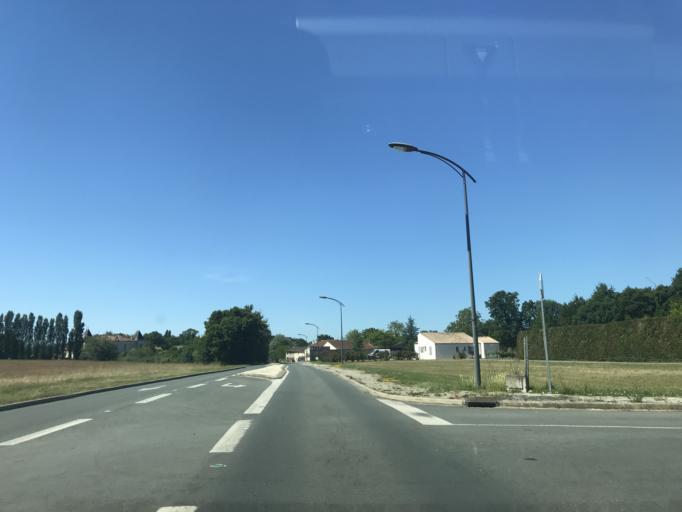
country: FR
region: Poitou-Charentes
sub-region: Departement de la Charente-Maritime
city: Gemozac
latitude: 45.5671
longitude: -0.7184
